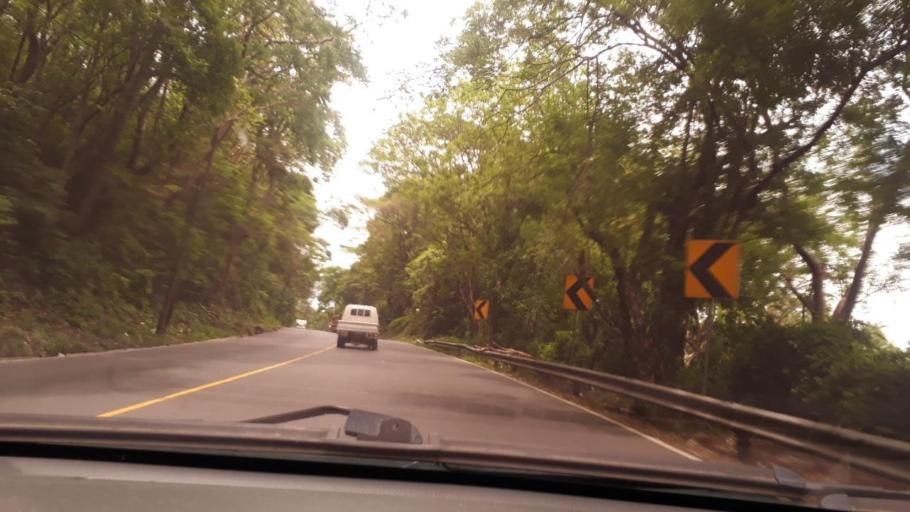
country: GT
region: Izabal
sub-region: Municipio de Los Amates
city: Los Amates
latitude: 15.2436
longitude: -89.1376
